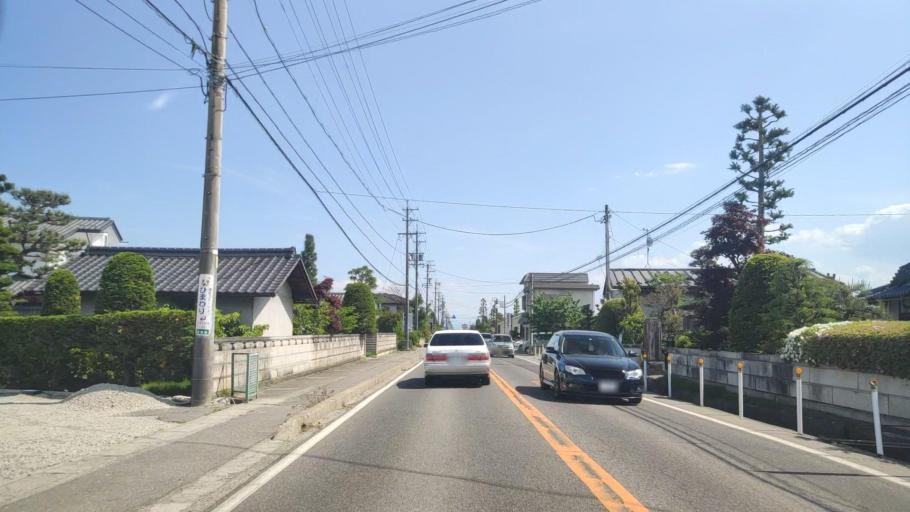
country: JP
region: Nagano
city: Hotaka
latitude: 36.3696
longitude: 137.8751
